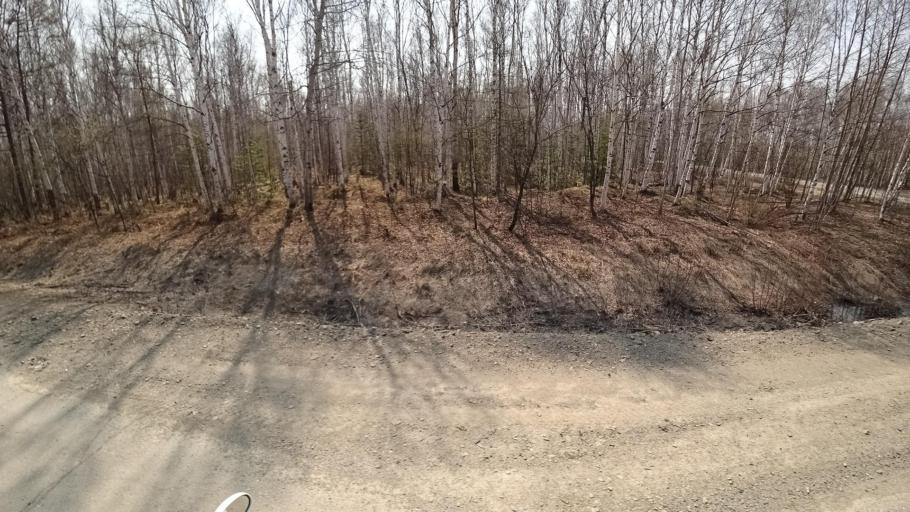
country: RU
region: Khabarovsk Krai
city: Selikhino
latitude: 50.3962
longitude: 137.3740
